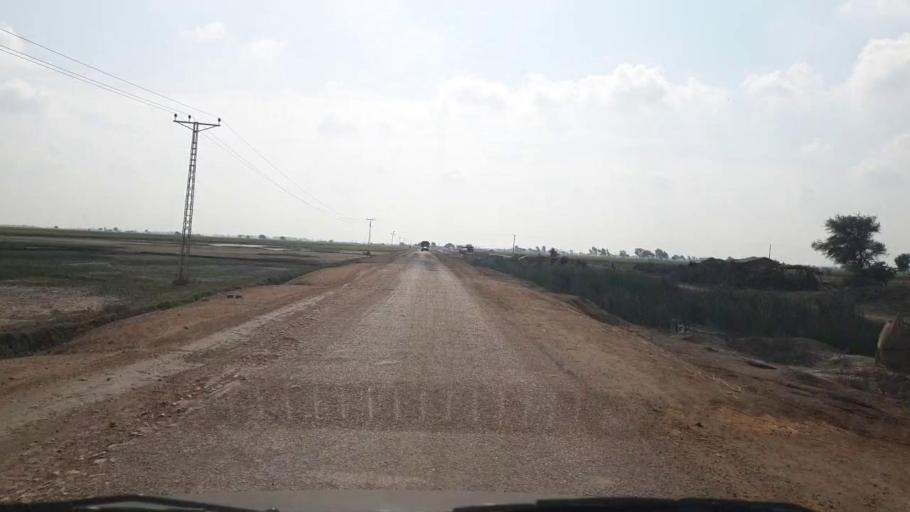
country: PK
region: Sindh
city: Kario
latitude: 24.6252
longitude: 68.5540
